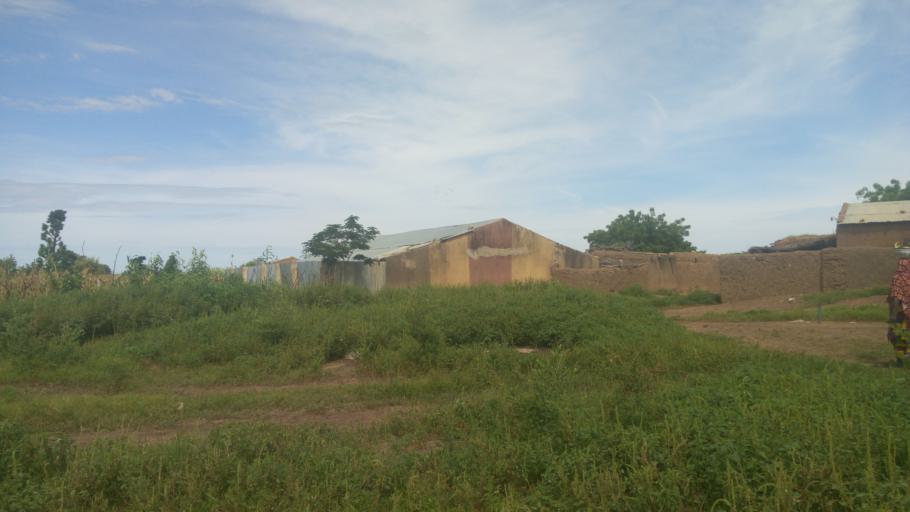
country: ML
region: Kayes
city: Yelimane
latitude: 14.8422
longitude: -10.7472
